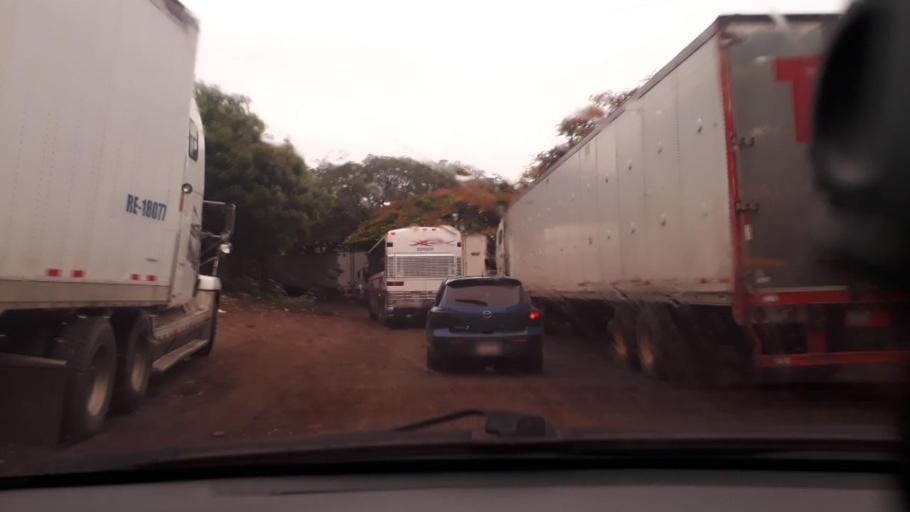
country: GT
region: Jutiapa
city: Atescatempa
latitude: 14.2170
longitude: -89.6923
